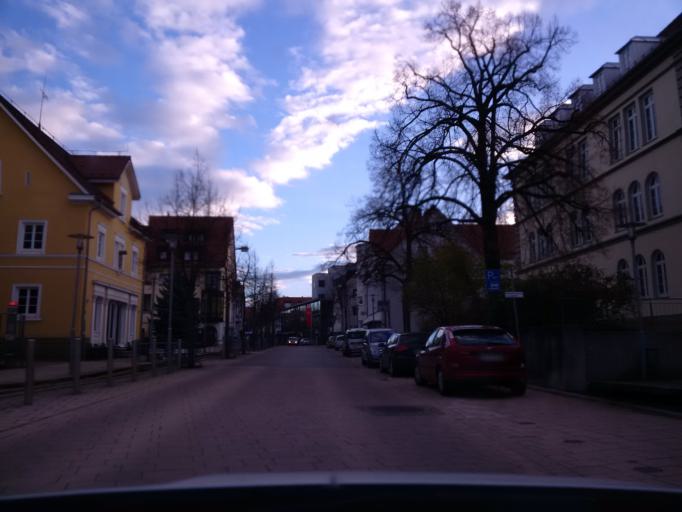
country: DE
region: Baden-Wuerttemberg
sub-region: Tuebingen Region
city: Laupheim
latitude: 48.2282
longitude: 9.8807
